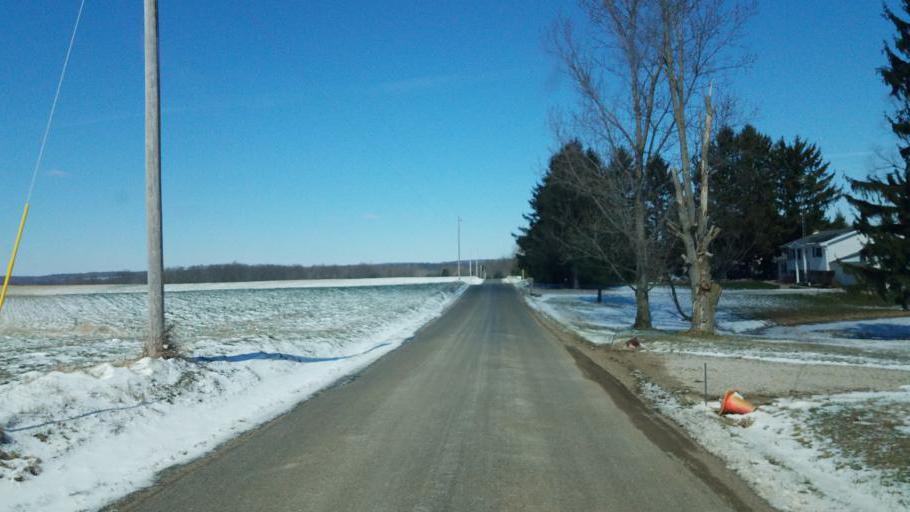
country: US
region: Ohio
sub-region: Richland County
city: Lexington
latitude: 40.6083
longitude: -82.6150
